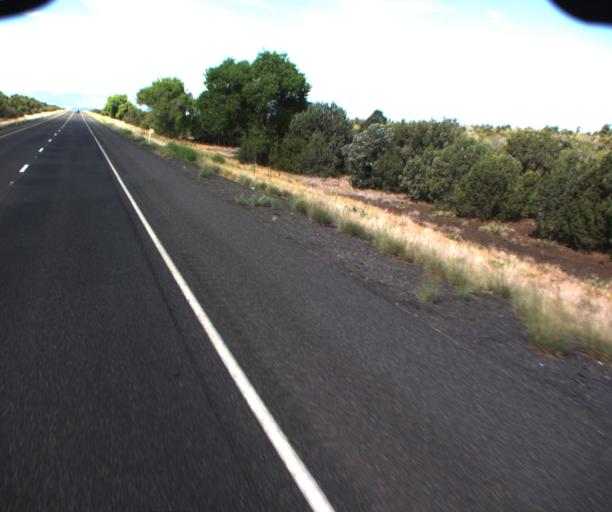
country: US
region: Arizona
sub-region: Yavapai County
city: Village of Oak Creek (Big Park)
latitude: 34.7493
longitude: -111.6786
